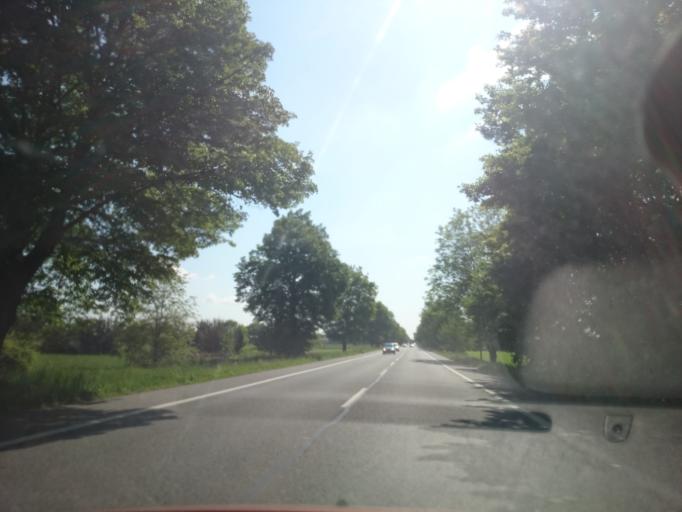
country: PL
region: Opole Voivodeship
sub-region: Powiat strzelecki
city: Izbicko
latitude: 50.5743
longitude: 18.1426
